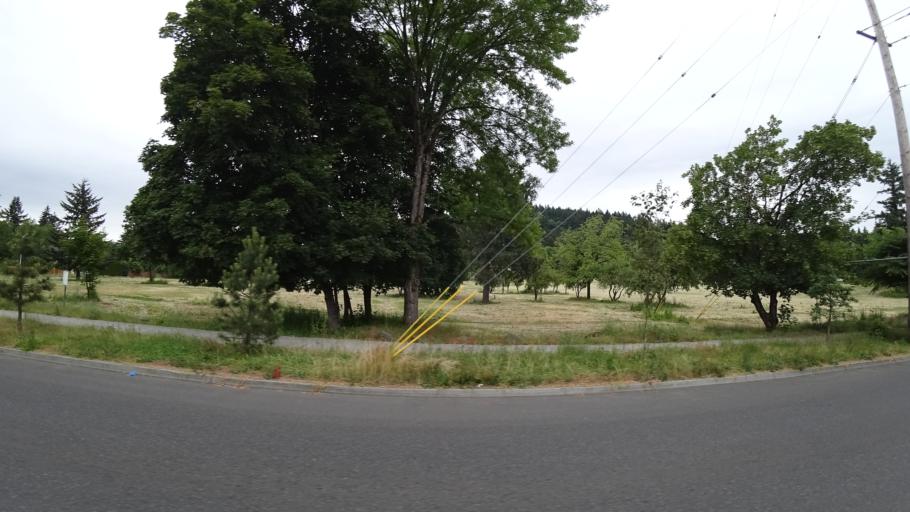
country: US
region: Oregon
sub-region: Clackamas County
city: Happy Valley
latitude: 45.4898
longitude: -122.5236
